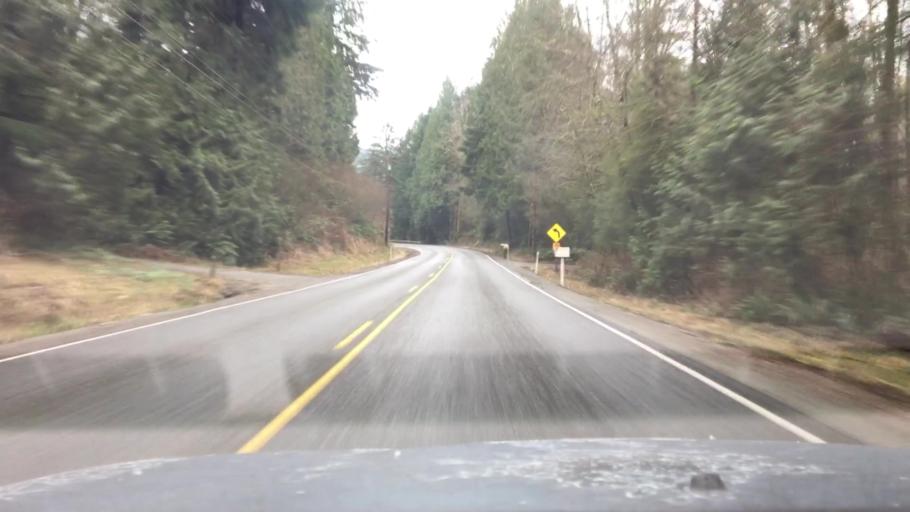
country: US
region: Washington
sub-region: Whatcom County
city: Sudden Valley
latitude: 48.6433
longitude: -122.3221
